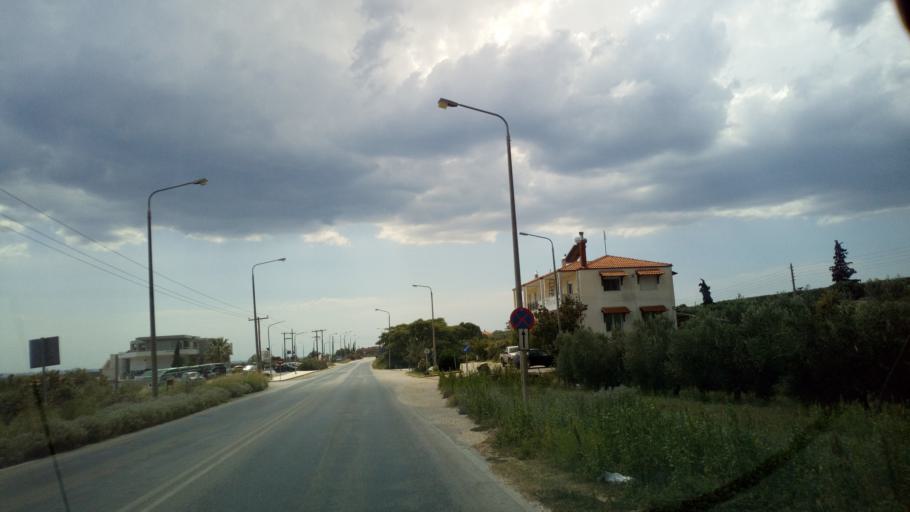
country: GR
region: Central Macedonia
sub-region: Nomos Chalkidikis
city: Ormylia
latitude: 40.2611
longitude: 23.5112
